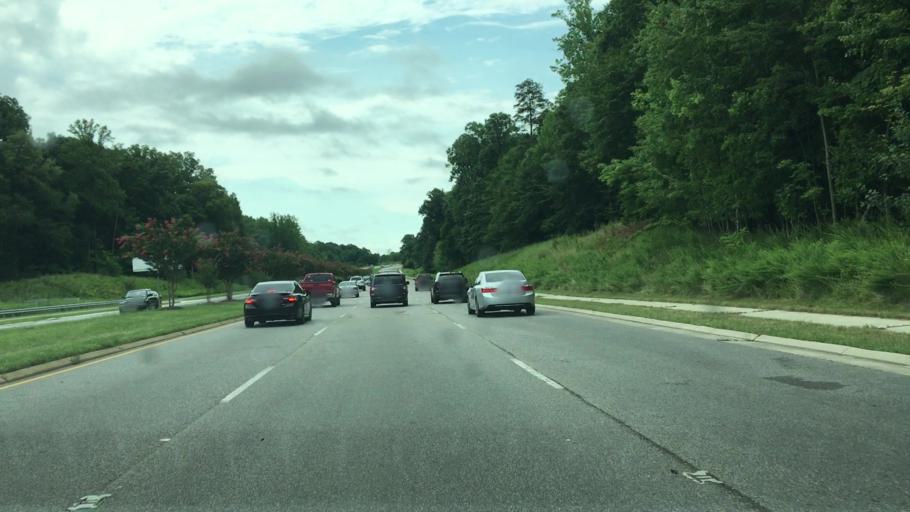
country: US
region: Virginia
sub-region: Prince William County
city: Dale City
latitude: 38.6587
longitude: -77.3232
